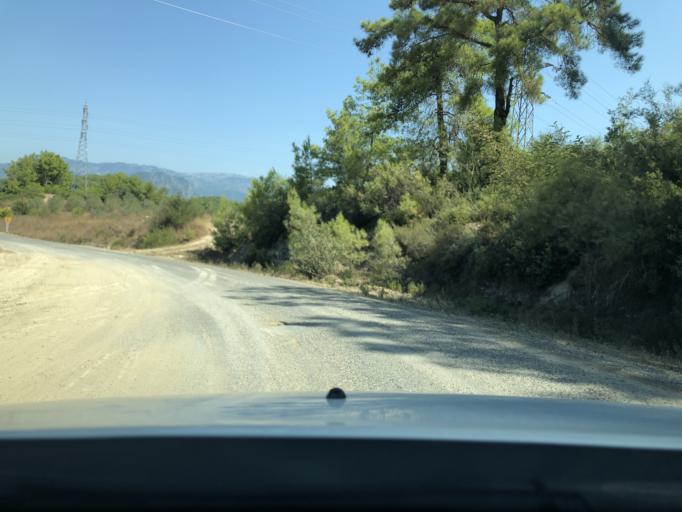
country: TR
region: Antalya
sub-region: Manavgat
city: Manavgat
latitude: 36.8225
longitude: 31.5080
